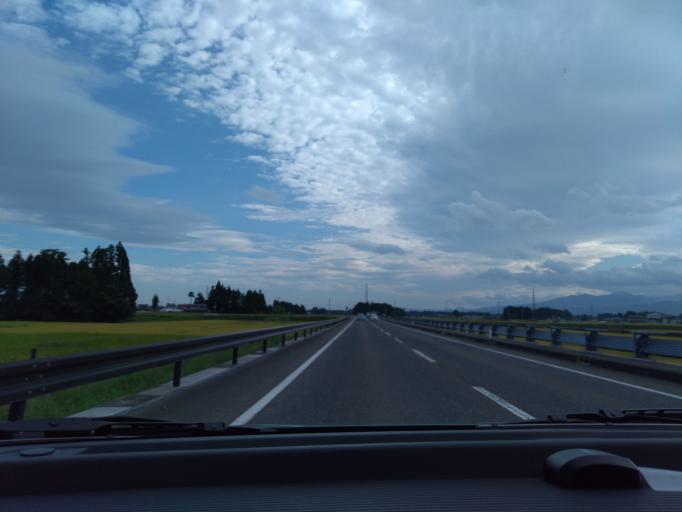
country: JP
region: Iwate
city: Hanamaki
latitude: 39.3475
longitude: 141.0524
